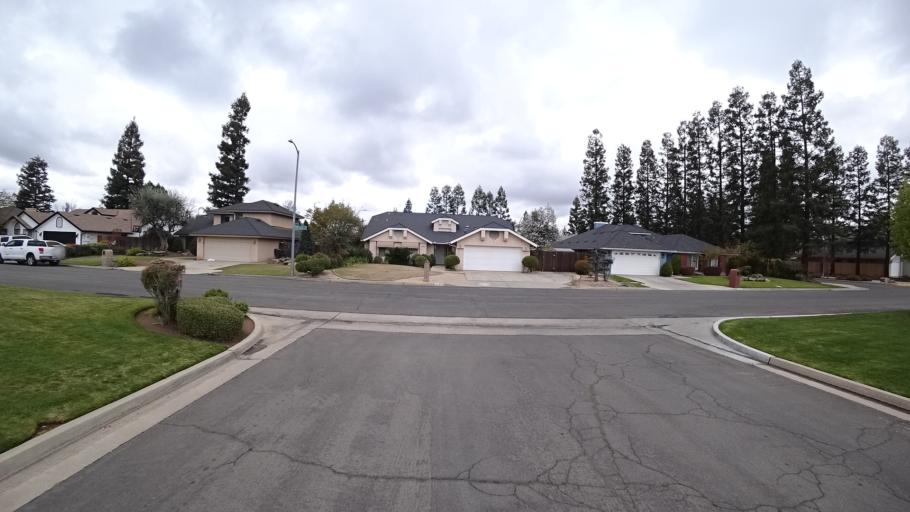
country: US
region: California
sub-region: Fresno County
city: Fresno
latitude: 36.8402
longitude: -119.8256
